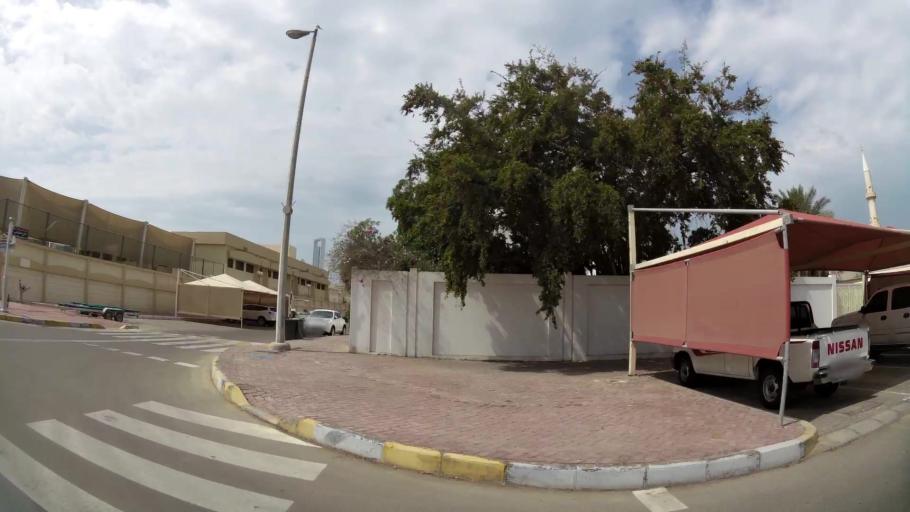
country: AE
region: Abu Dhabi
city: Abu Dhabi
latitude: 24.4569
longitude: 54.3441
